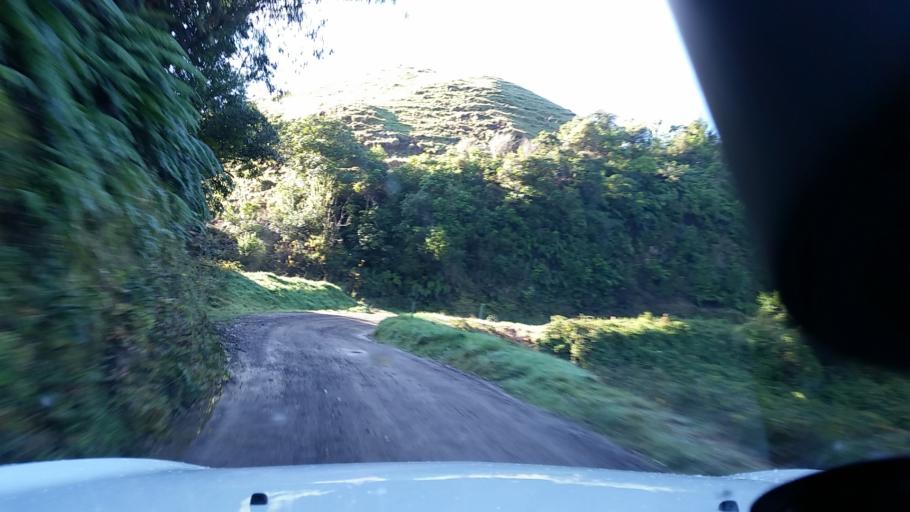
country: NZ
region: Bay of Plenty
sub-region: Kawerau District
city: Kawerau
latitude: -38.0029
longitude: 176.6043
